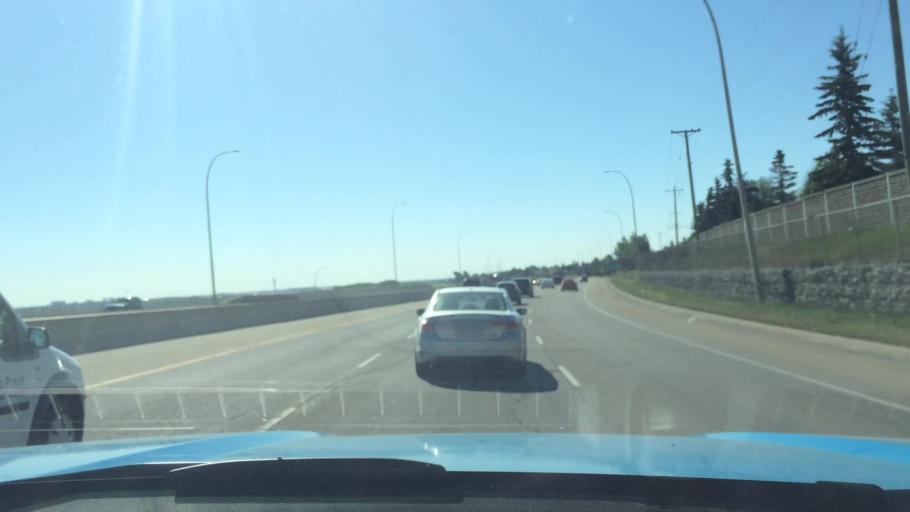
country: CA
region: Alberta
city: Calgary
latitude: 51.1365
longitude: -114.0763
